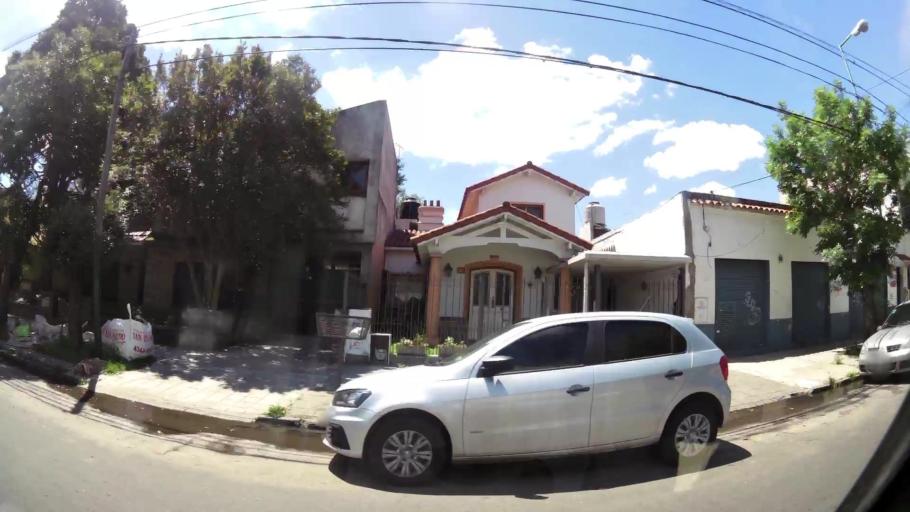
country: AR
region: Buenos Aires
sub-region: Partido de Lomas de Zamora
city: Lomas de Zamora
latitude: -34.7396
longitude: -58.4016
